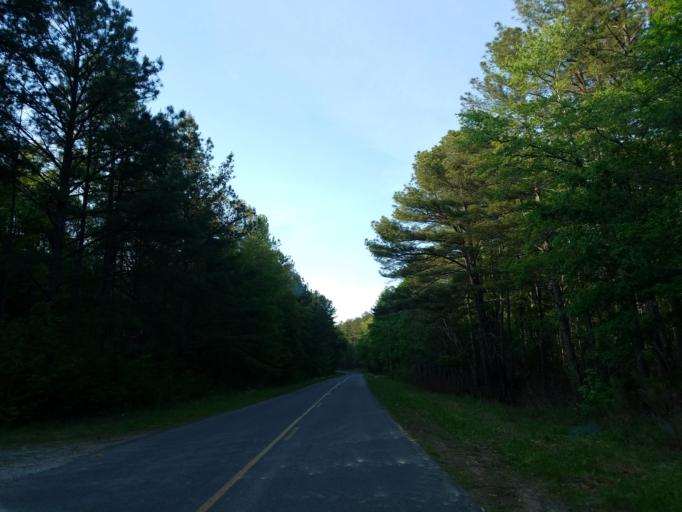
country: US
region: Georgia
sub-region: Gordon County
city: Calhoun
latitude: 34.6060
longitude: -85.0813
